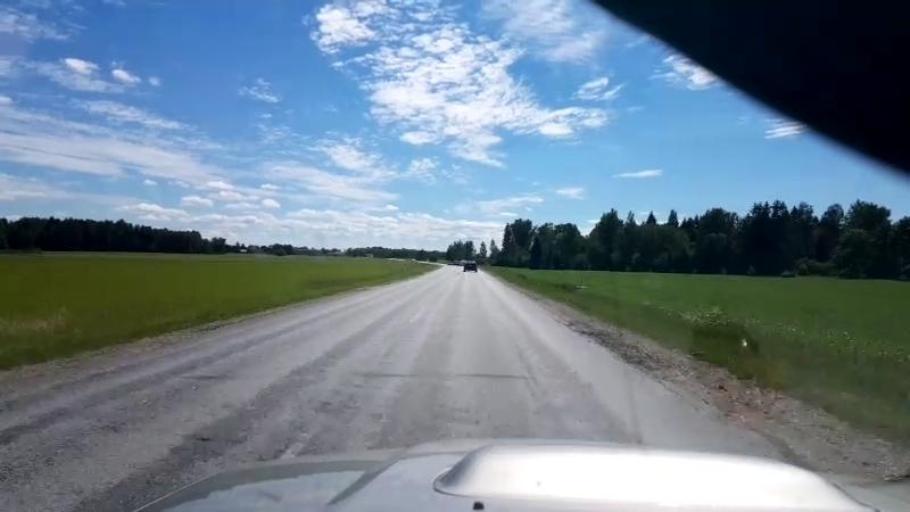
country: EE
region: Jogevamaa
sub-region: Jogeva linn
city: Jogeva
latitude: 58.8286
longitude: 26.2866
